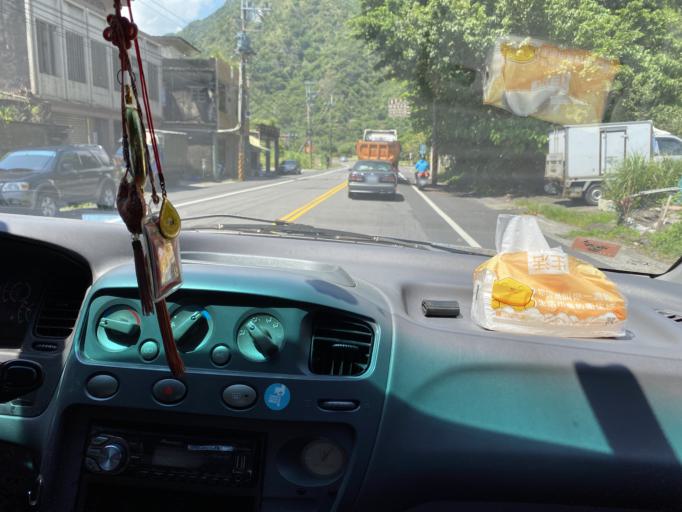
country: TW
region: Taiwan
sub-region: Yilan
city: Yilan
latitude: 24.9420
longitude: 121.8975
